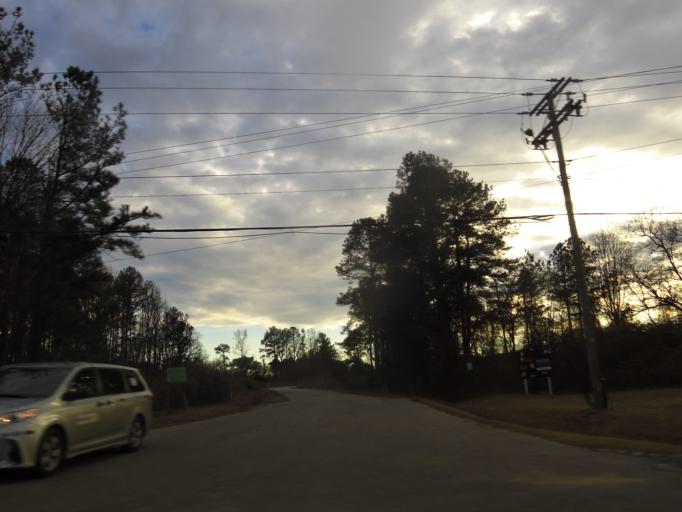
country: US
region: North Carolina
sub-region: Nash County
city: Rocky Mount
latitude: 35.9159
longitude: -77.8044
